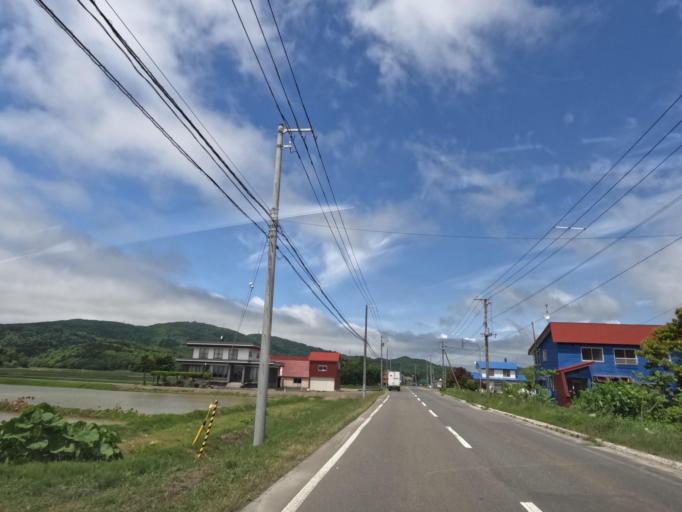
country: JP
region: Hokkaido
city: Tobetsu
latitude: 43.2770
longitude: 141.5344
